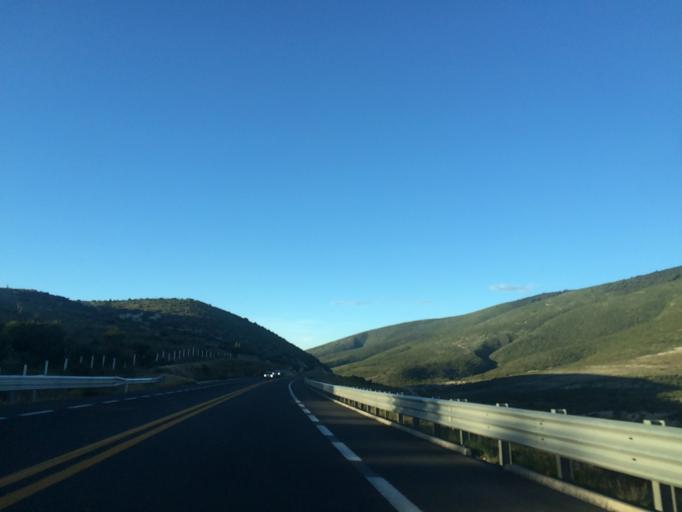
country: MX
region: Puebla
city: Morelos Canada
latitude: 18.6843
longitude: -97.4601
